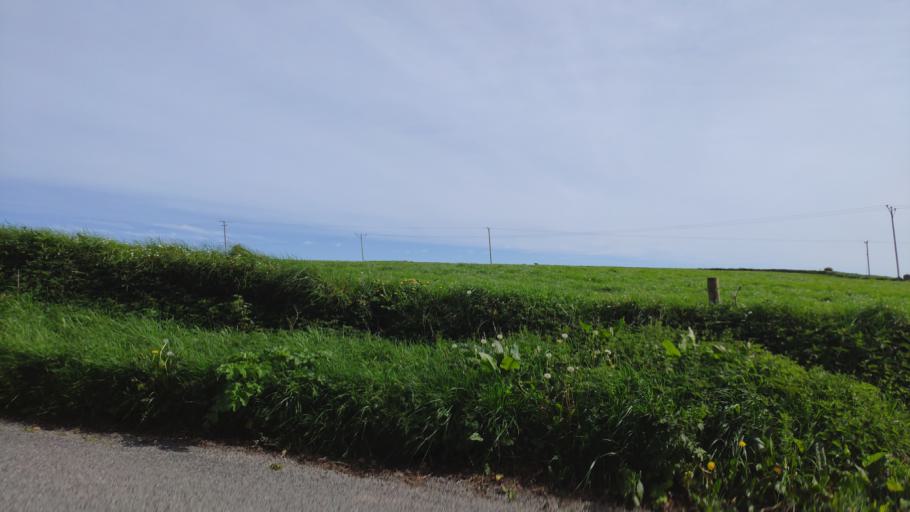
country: IE
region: Munster
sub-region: County Cork
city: Blarney
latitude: 51.9552
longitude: -8.5073
